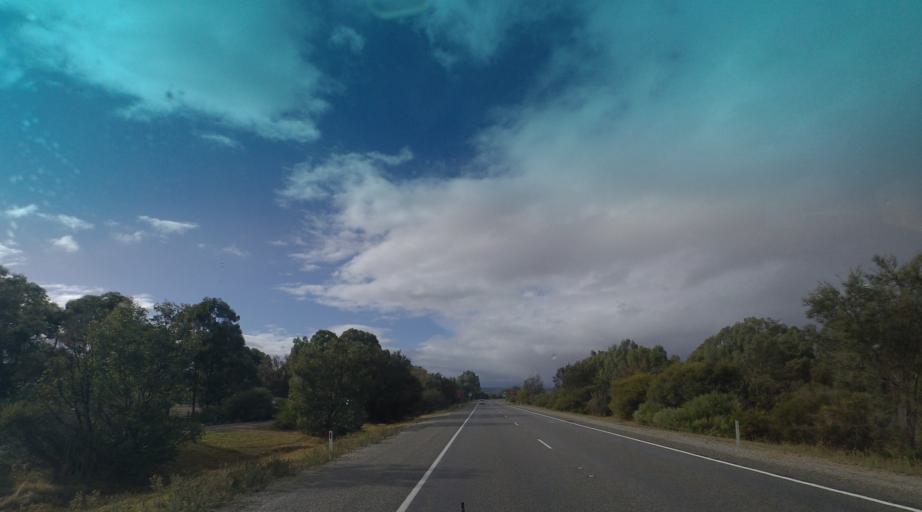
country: AU
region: Western Australia
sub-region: Serpentine-Jarrahdale
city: Oakford
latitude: -32.2027
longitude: 115.9665
